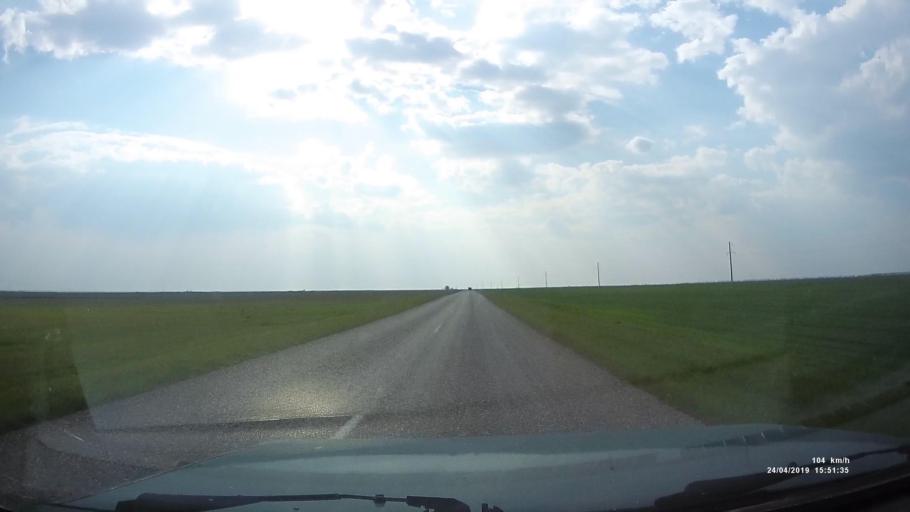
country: RU
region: Kalmykiya
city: Yashalta
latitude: 46.6044
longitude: 42.6074
